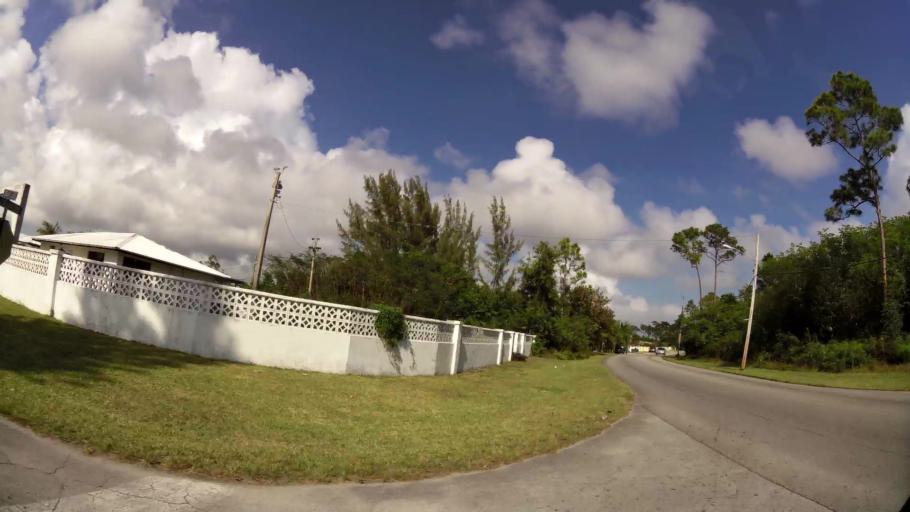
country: BS
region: Freeport
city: Lucaya
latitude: 26.5266
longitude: -78.6816
